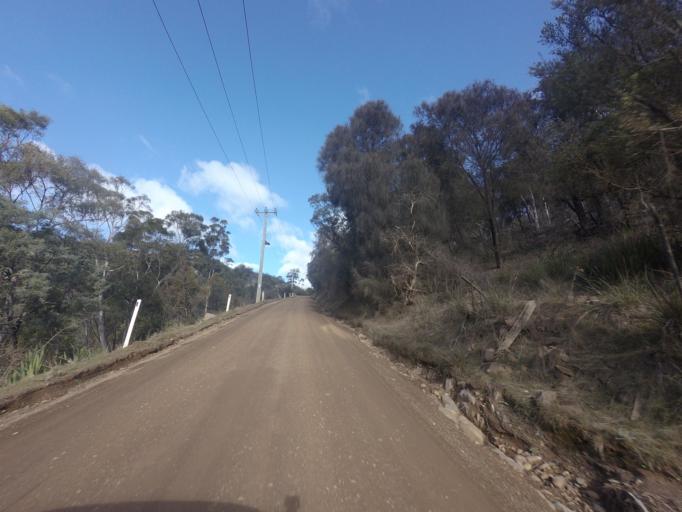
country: AU
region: Tasmania
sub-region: Derwent Valley
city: New Norfolk
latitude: -42.8174
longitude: 147.1279
